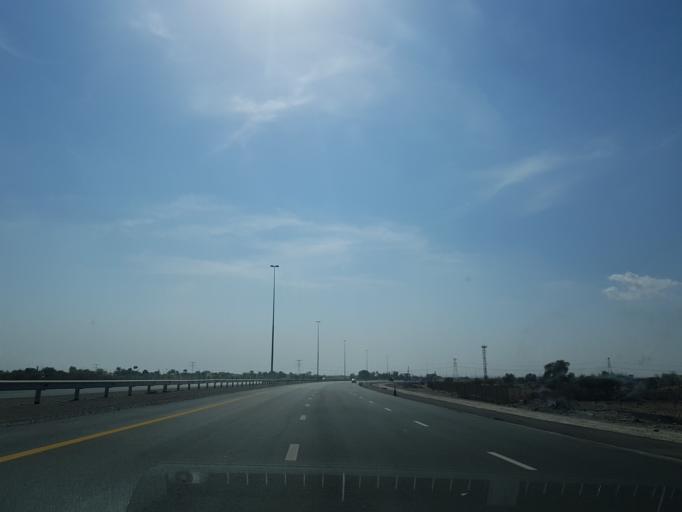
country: AE
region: Ra's al Khaymah
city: Ras al-Khaimah
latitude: 25.7029
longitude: 55.9933
